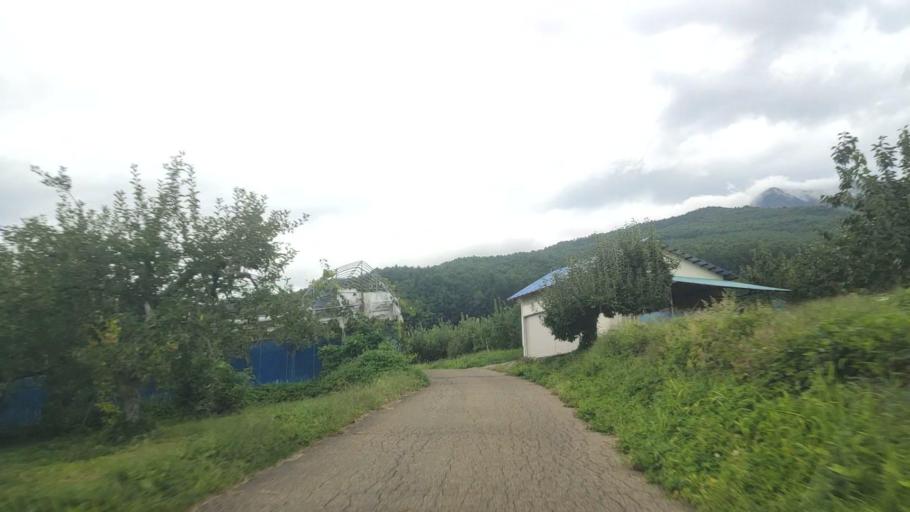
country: JP
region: Nagano
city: Nakano
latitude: 36.7775
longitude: 138.3861
